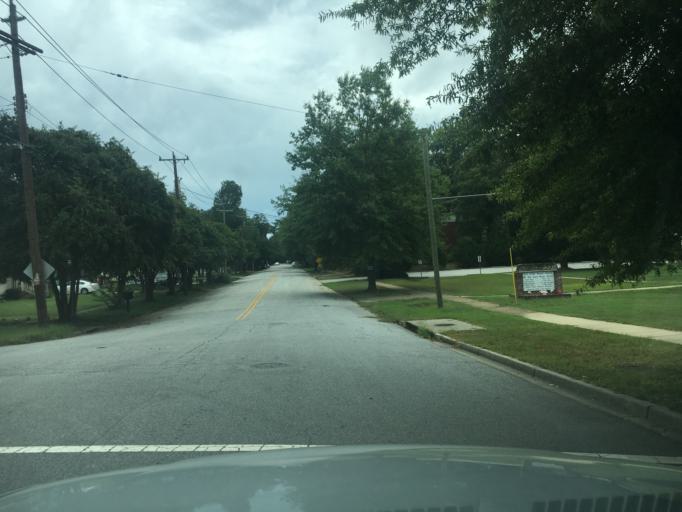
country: US
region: South Carolina
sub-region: Greenville County
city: Greenville
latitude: 34.8586
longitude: -82.4096
